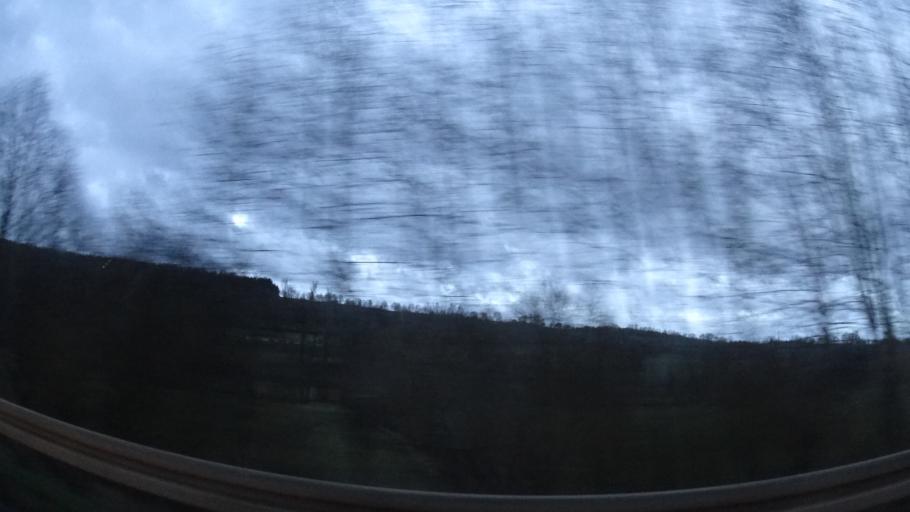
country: DE
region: Bavaria
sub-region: Regierungsbezirk Unterfranken
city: Motten
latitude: 50.4514
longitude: 9.8066
